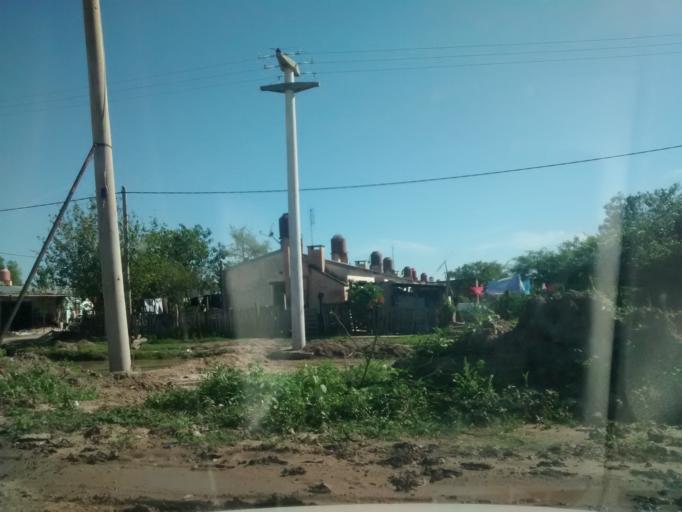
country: AR
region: Chaco
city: Fontana
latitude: -27.4018
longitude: -58.9849
